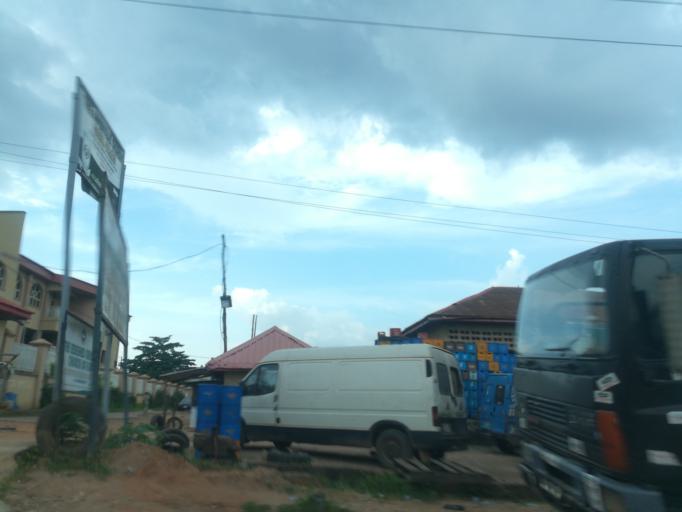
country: NG
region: Oyo
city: Ibadan
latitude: 7.4269
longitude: 3.8845
